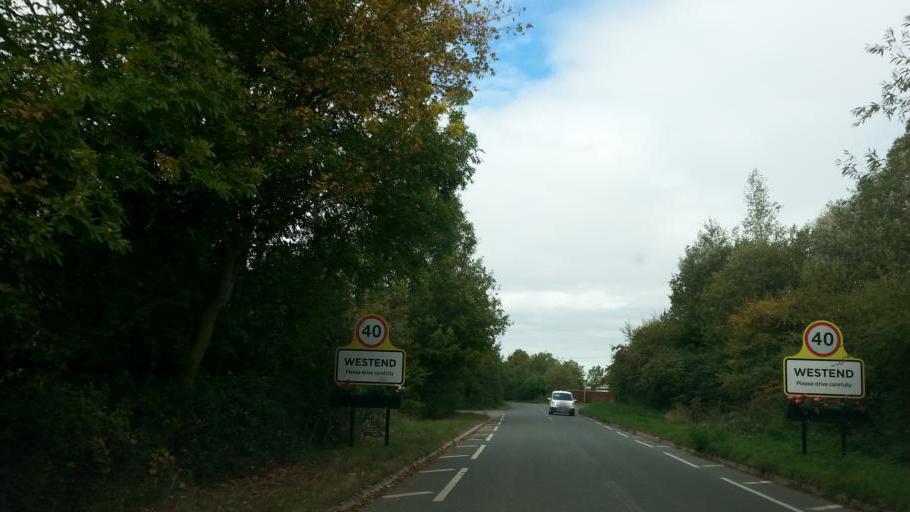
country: GB
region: England
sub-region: Gloucestershire
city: Stonehouse
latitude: 51.7572
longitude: -2.3134
